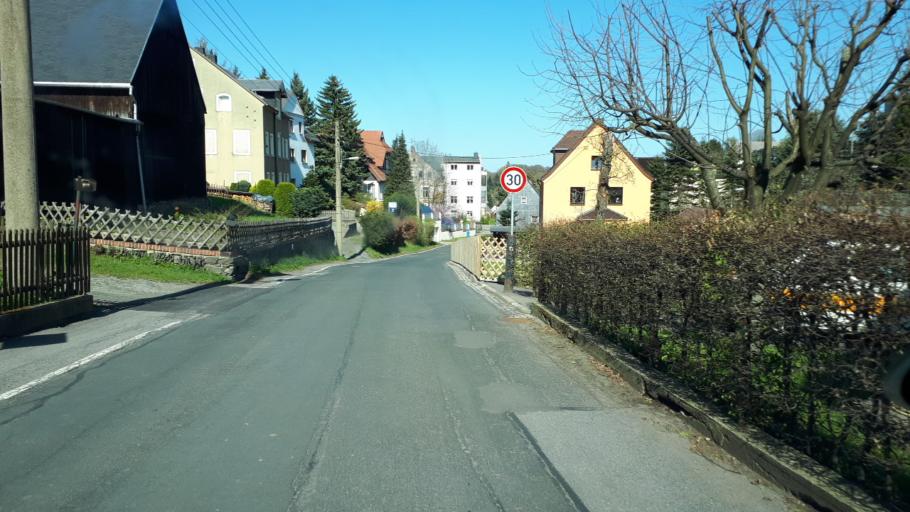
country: DE
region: Saxony
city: Burkhardtsdorf
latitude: 50.7639
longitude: 12.9435
